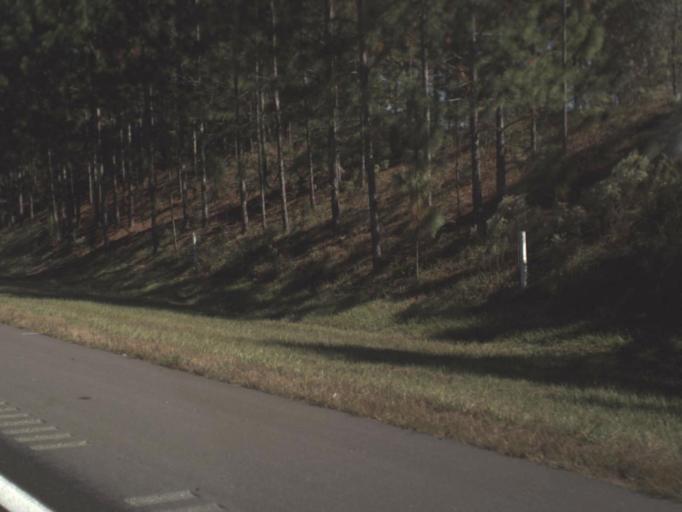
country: US
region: Florida
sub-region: Hernando County
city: Spring Hill
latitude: 28.4890
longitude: -82.4834
